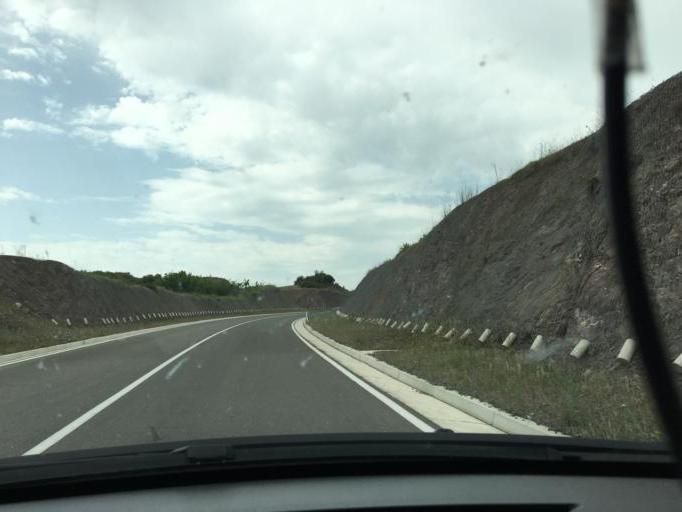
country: MK
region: Gevgelija
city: Miravci
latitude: 41.3011
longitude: 22.4410
